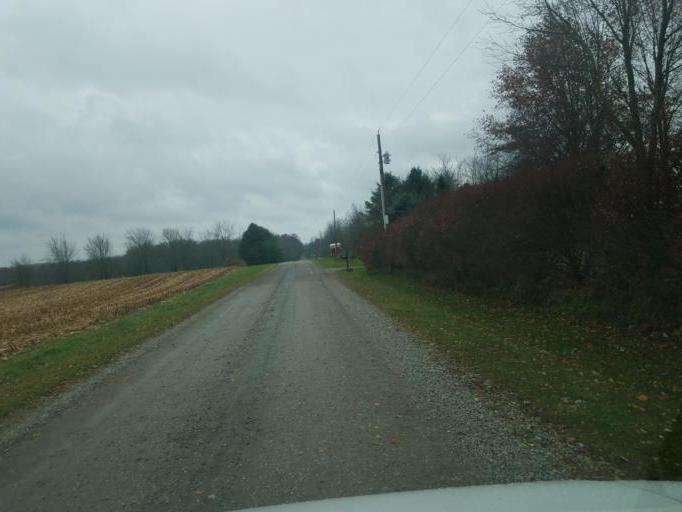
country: US
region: Ohio
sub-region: Morrow County
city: Mount Gilead
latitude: 40.5295
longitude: -82.7015
